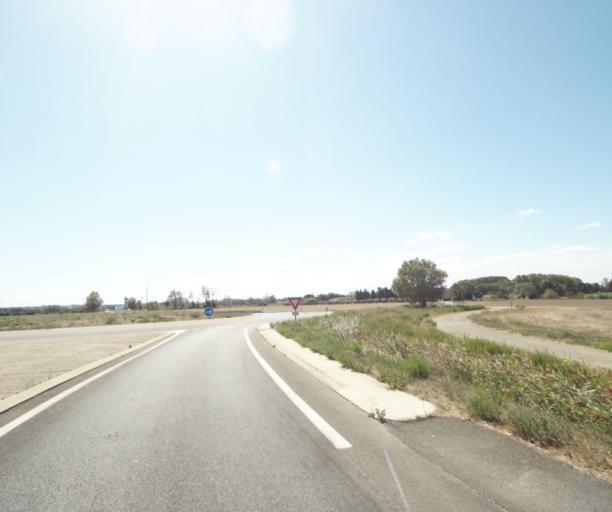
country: FR
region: Languedoc-Roussillon
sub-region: Departement du Gard
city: Rodilhan
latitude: 43.8254
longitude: 4.4198
